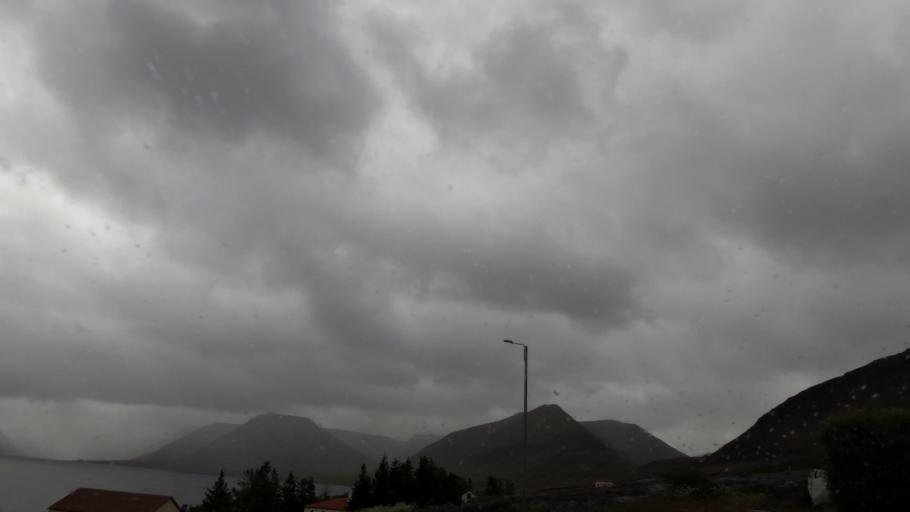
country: IS
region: Westfjords
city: Isafjoerdur
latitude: 65.8718
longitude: -23.4826
